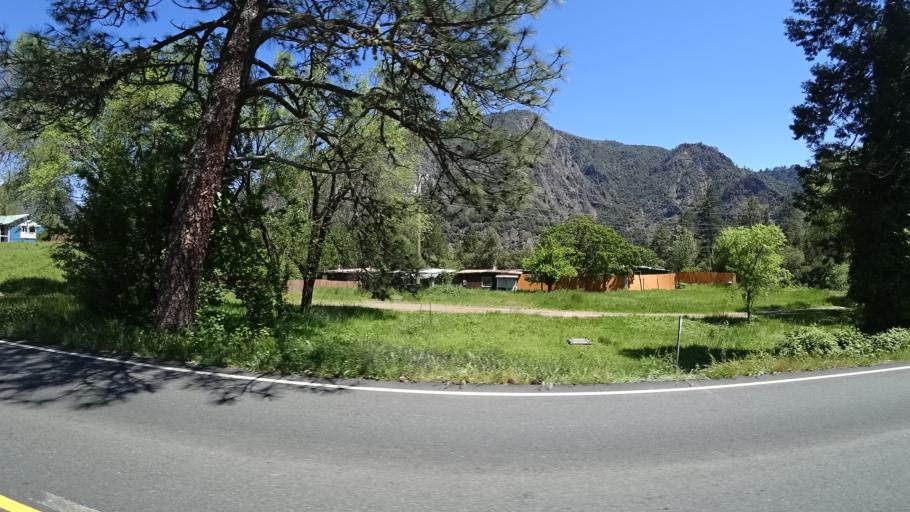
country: US
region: California
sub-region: Humboldt County
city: Willow Creek
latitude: 40.8295
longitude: -123.4876
